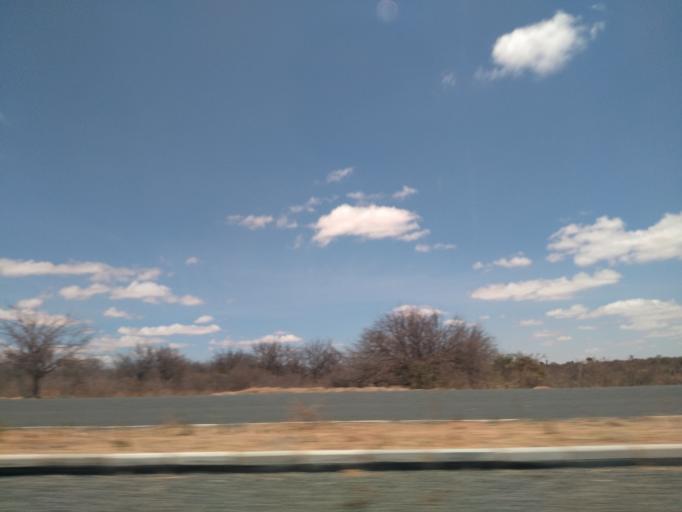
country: TZ
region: Dodoma
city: Kisasa
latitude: -6.1733
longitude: 35.8363
